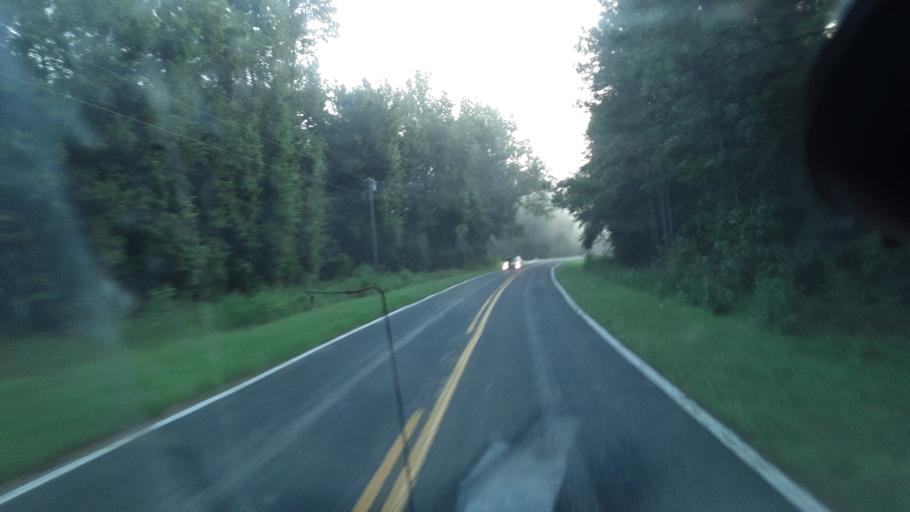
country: US
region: South Carolina
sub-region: Clarendon County
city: Manning
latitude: 33.7461
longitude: -80.0757
